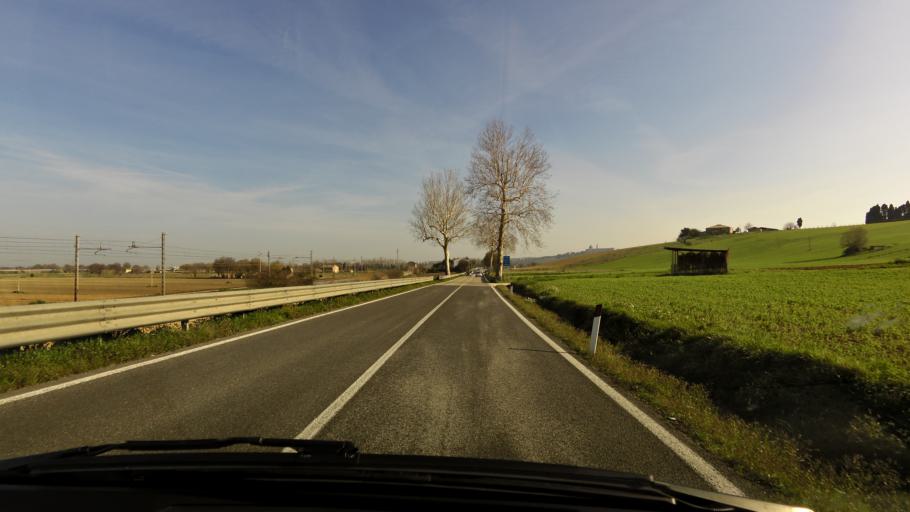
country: IT
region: The Marches
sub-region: Provincia di Ancona
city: Villa Musone
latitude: 43.4698
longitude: 13.5993
